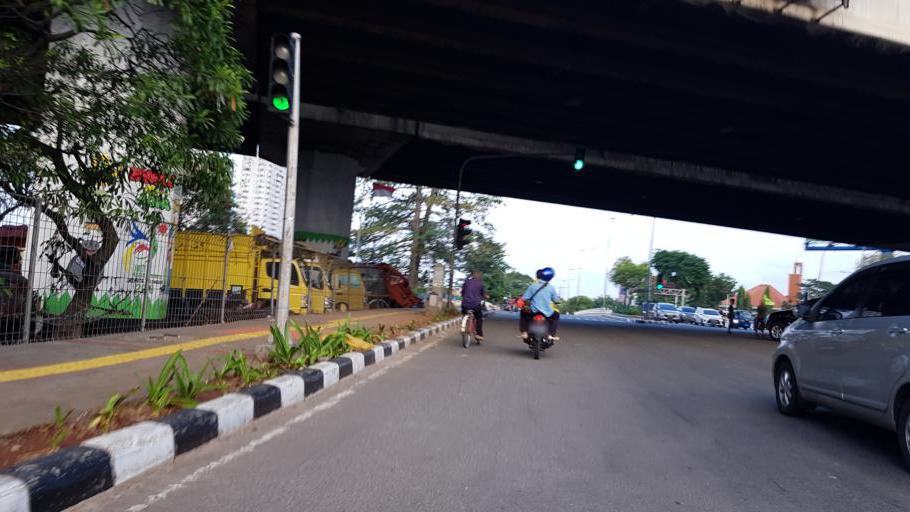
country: ID
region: Jakarta Raya
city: Jakarta
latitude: -6.1432
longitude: 106.7886
